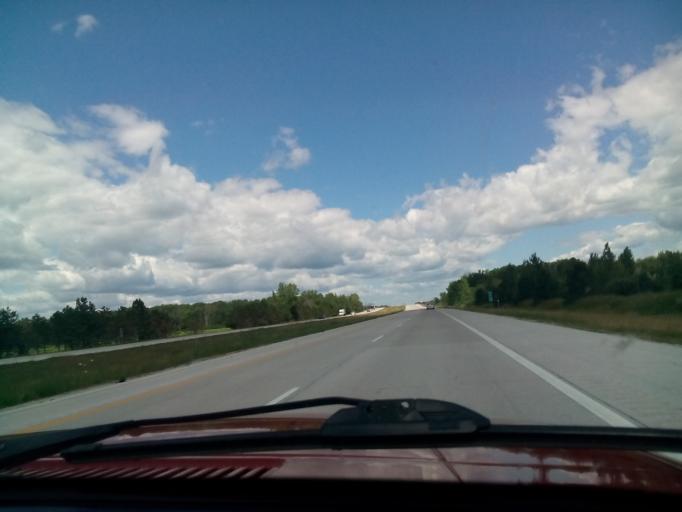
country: US
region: Michigan
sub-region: Bay County
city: Pinconning
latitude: 43.8898
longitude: -84.0198
